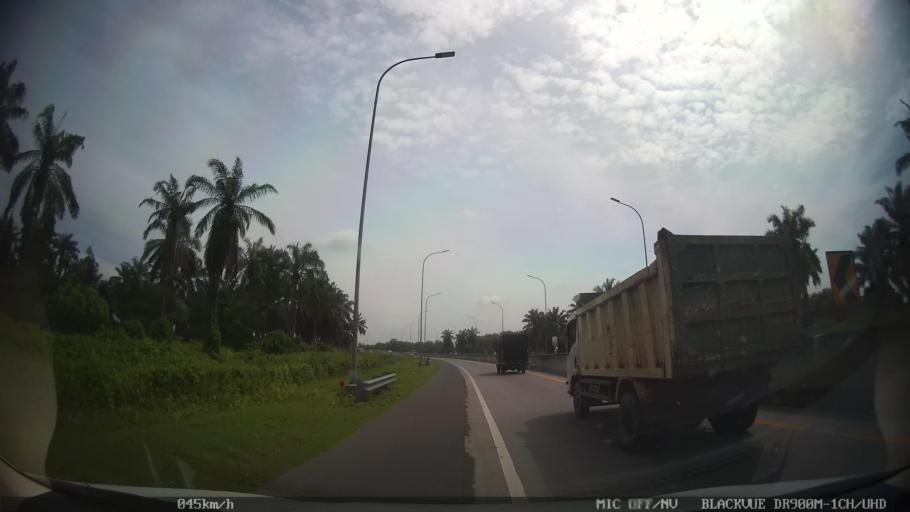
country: ID
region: North Sumatra
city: Medan
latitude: 3.6322
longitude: 98.6348
